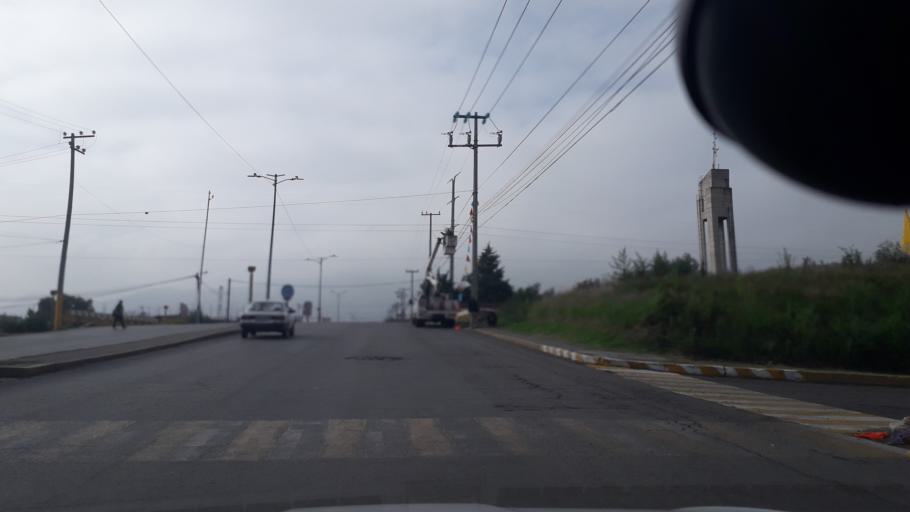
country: MX
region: Mexico
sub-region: Jaltenco
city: Alborada Jaltenco
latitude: 19.6463
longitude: -99.0777
